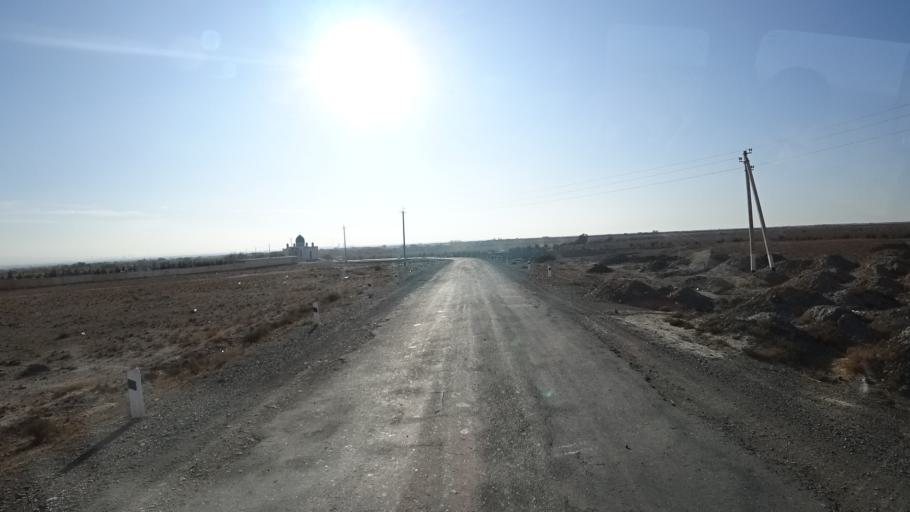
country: UZ
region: Navoiy
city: Beshrabot
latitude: 40.2205
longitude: 65.3869
